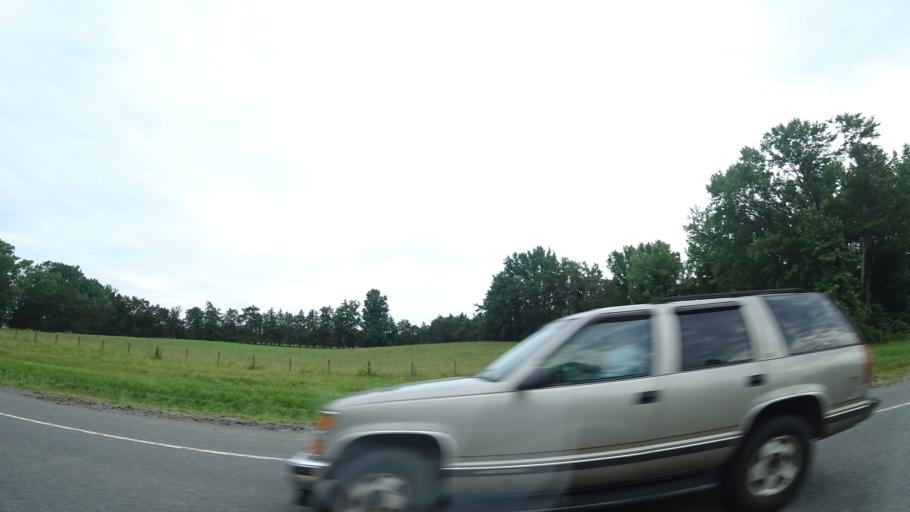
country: US
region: Virginia
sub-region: Spotsylvania County
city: Spotsylvania Courthouse
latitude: 38.1612
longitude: -77.6633
